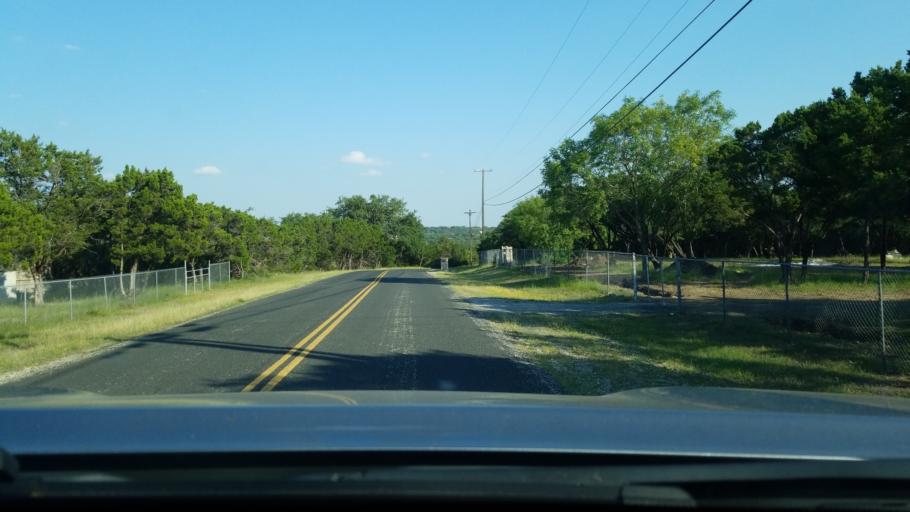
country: US
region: Texas
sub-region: Comal County
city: Bulverde
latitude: 29.7084
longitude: -98.4381
